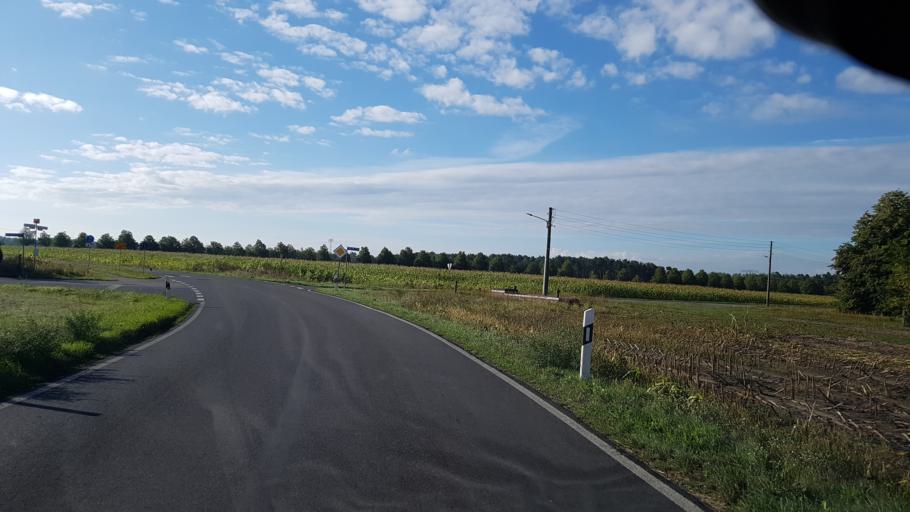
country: DE
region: Brandenburg
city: Spremberg
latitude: 51.5289
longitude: 14.3015
